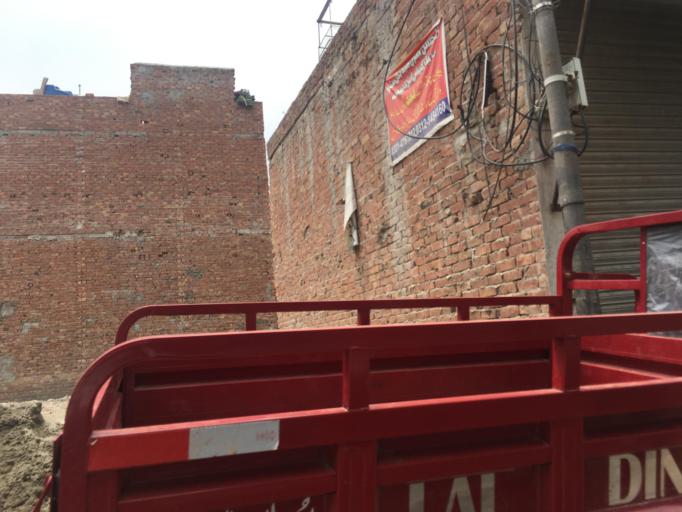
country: PK
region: Punjab
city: Lahore
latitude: 31.6136
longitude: 74.3508
